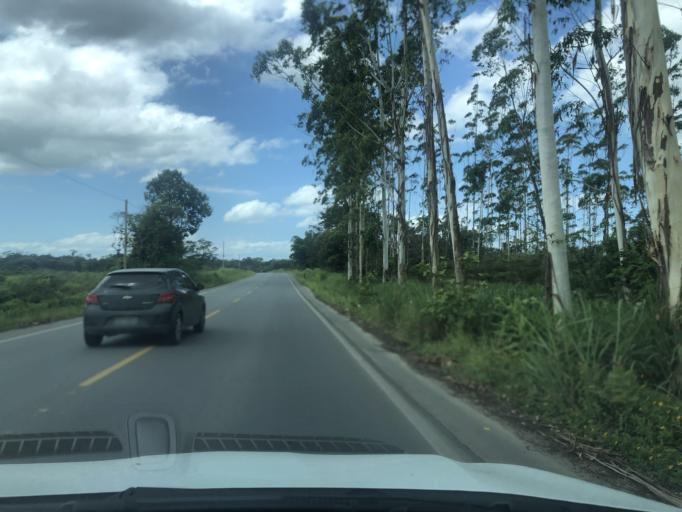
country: BR
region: Santa Catarina
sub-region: Joinville
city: Joinville
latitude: -26.4058
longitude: -48.7584
